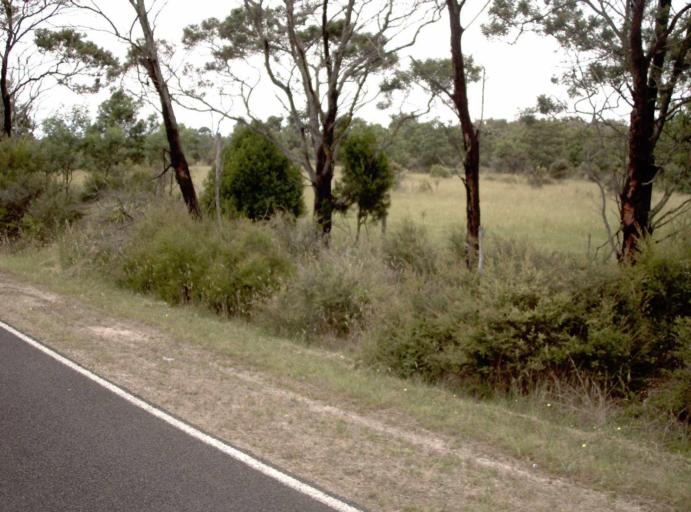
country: AU
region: Victoria
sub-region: Latrobe
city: Traralgon
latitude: -38.5041
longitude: 146.8389
